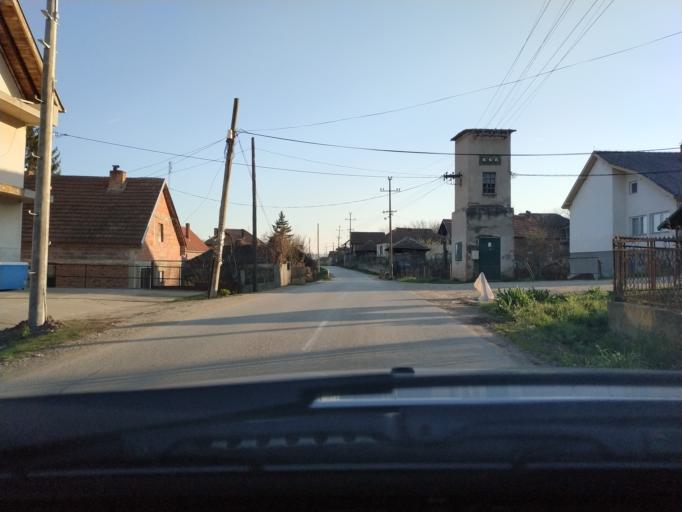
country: RS
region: Central Serbia
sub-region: Nisavski Okrug
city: Aleksinac
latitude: 43.5106
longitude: 21.7979
